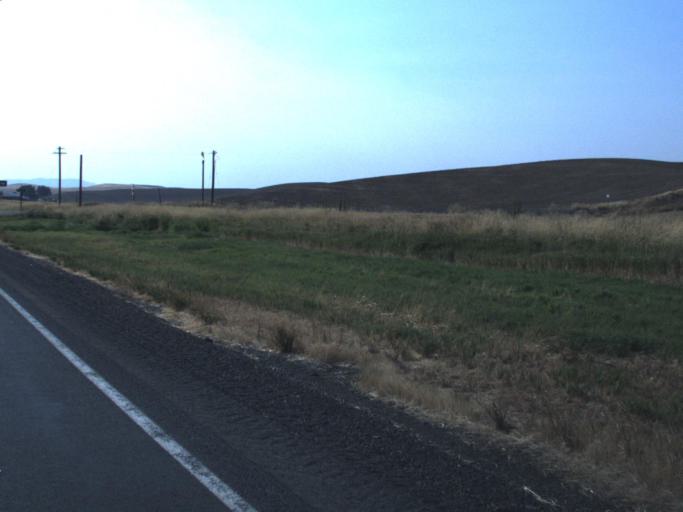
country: US
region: Washington
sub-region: Whitman County
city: Colfax
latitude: 47.0391
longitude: -117.1545
